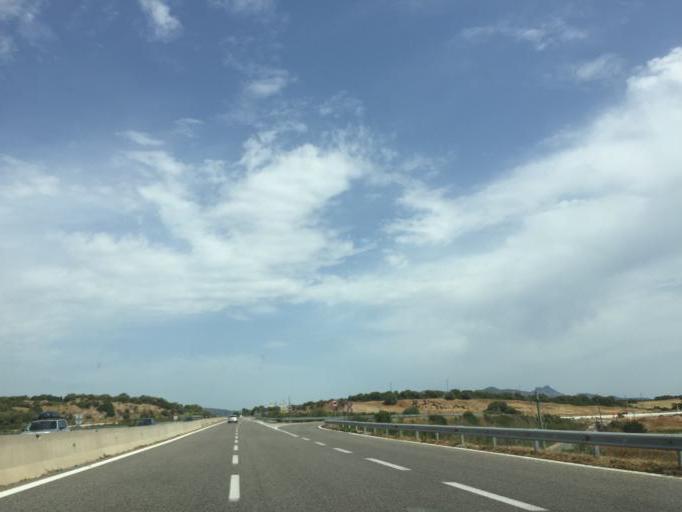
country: IT
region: Sardinia
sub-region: Provincia di Olbia-Tempio
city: Olbia
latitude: 40.8910
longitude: 9.4892
